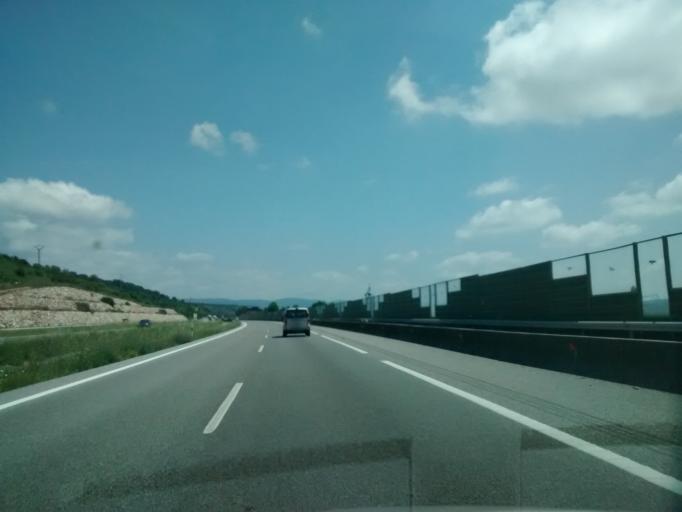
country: ES
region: Castille and Leon
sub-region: Provincia de Leon
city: Congosto
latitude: 42.5943
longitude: -6.5113
